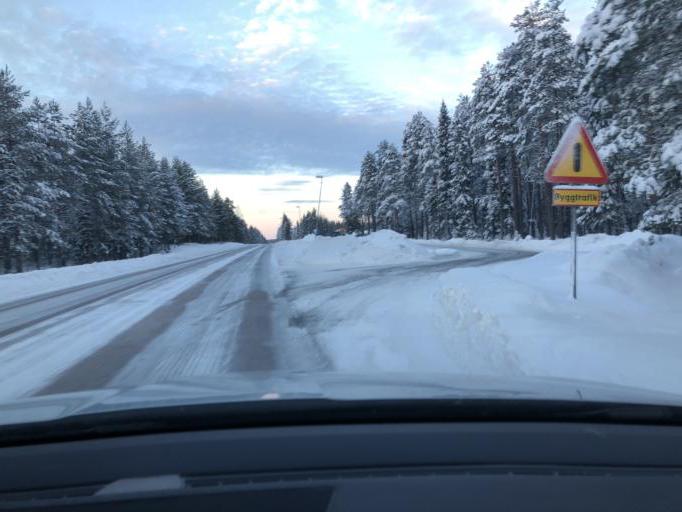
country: SE
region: Norrbotten
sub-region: Lulea Kommun
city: Bergnaset
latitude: 65.6252
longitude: 22.1228
